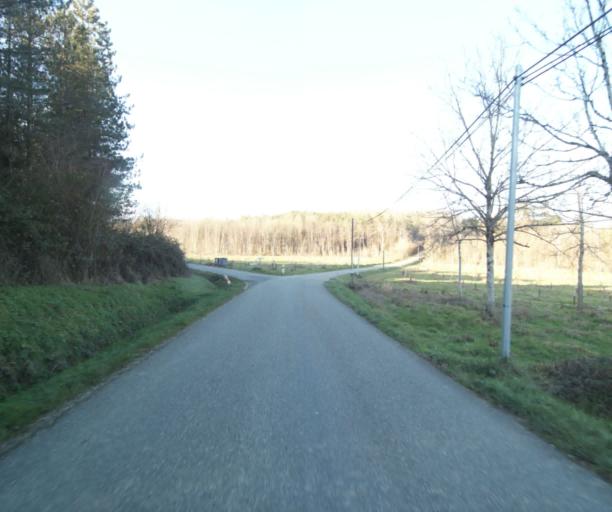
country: FR
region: Midi-Pyrenees
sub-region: Departement du Tarn-et-Garonne
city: Moissac
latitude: 44.1248
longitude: 1.1004
